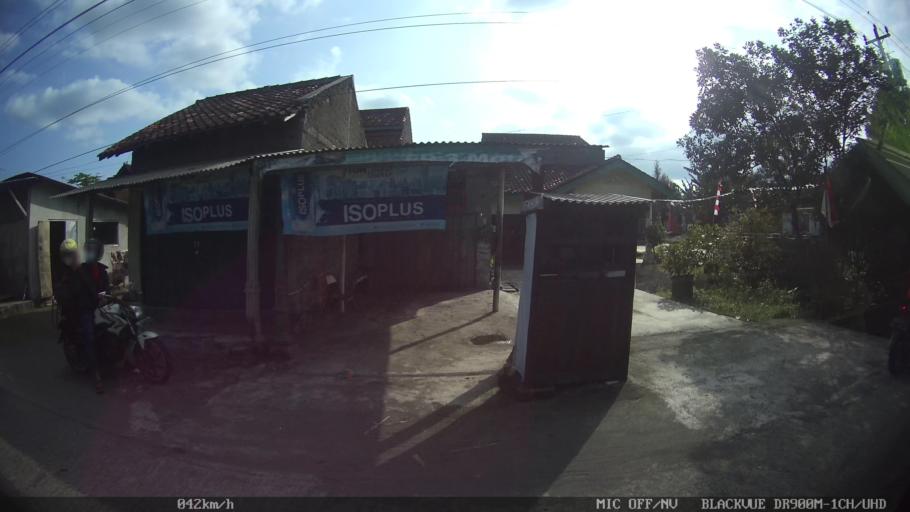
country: ID
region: Central Java
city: Candi Prambanan
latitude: -7.6945
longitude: 110.4634
